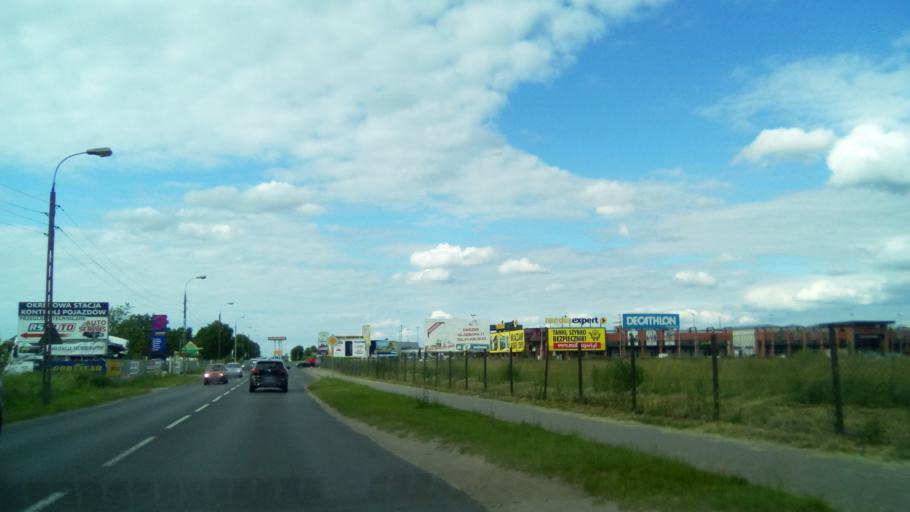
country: PL
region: Greater Poland Voivodeship
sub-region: Powiat gnieznienski
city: Gniezno
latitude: 52.5576
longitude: 17.6076
